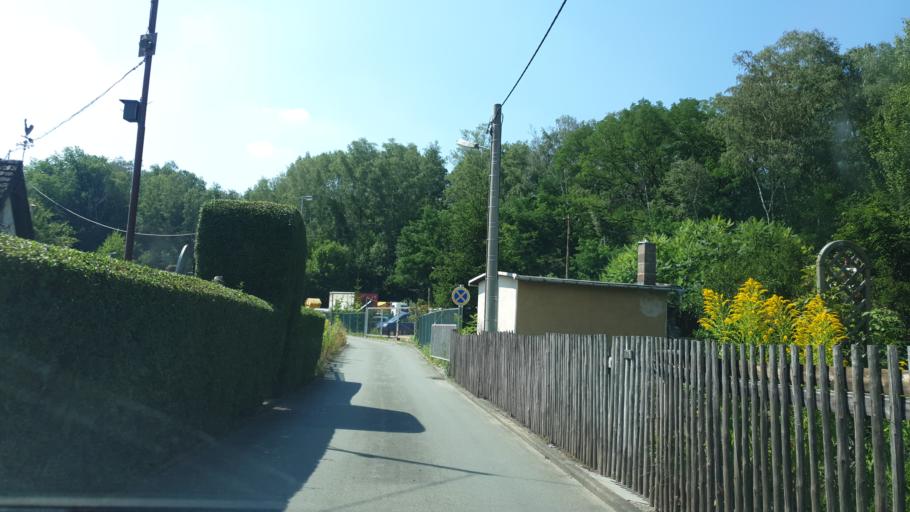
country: DE
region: Saxony
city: Gersdorf
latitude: 50.7469
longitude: 12.7097
